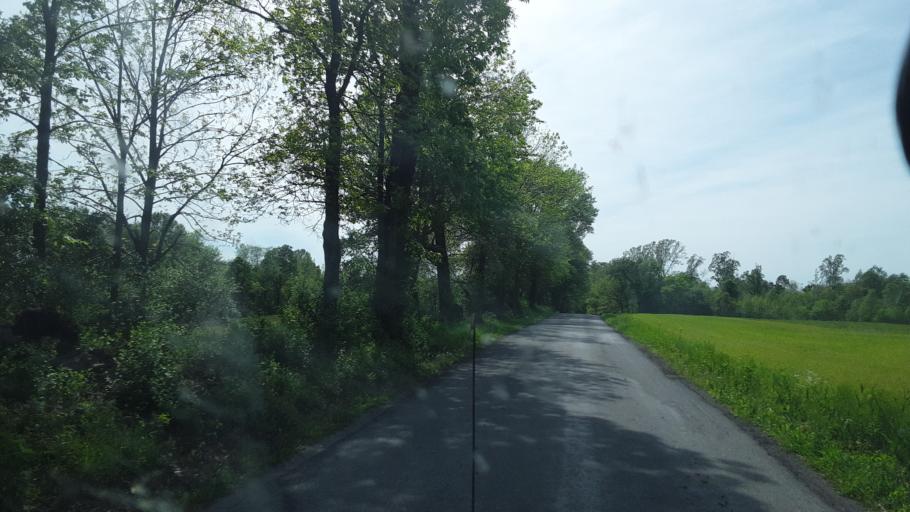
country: US
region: Illinois
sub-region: Jackson County
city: Carbondale
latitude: 37.6800
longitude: -89.2633
